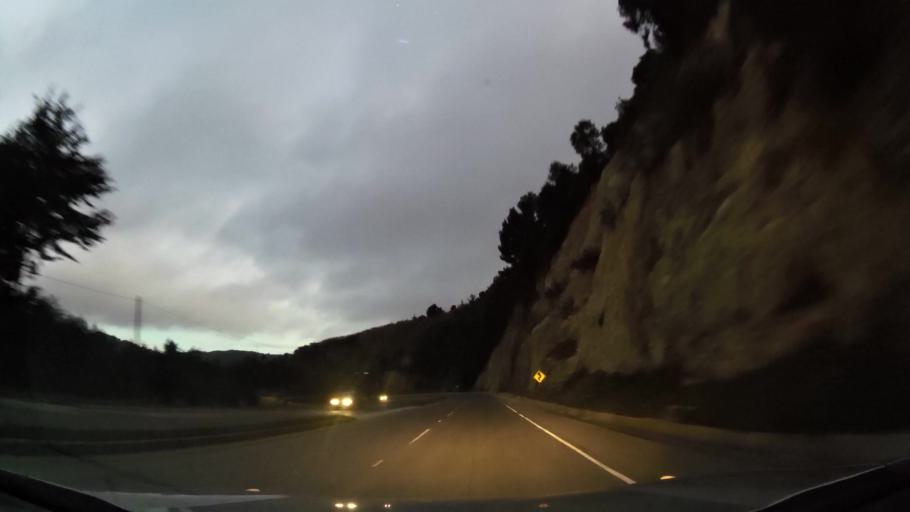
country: GT
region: Chimaltenango
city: Santa Apolonia
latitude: 14.8155
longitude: -90.9969
